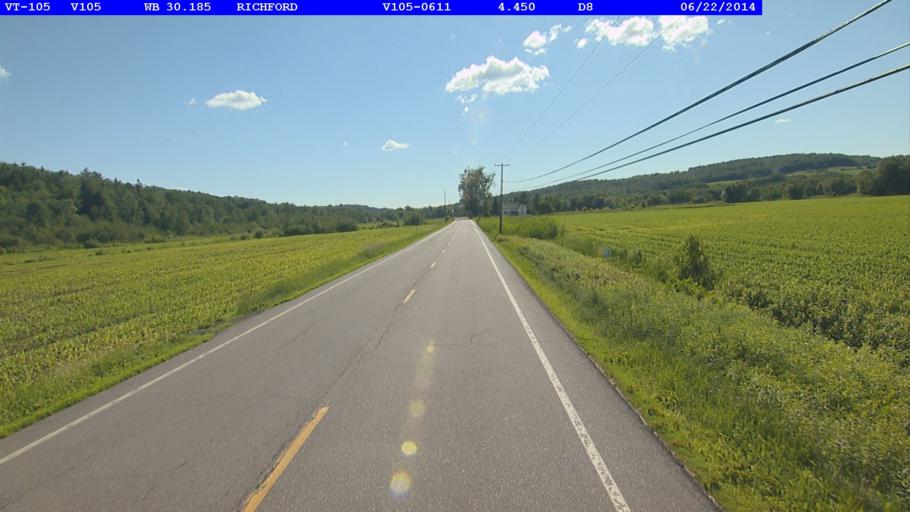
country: US
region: Vermont
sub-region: Franklin County
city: Richford
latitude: 44.9948
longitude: -72.6320
